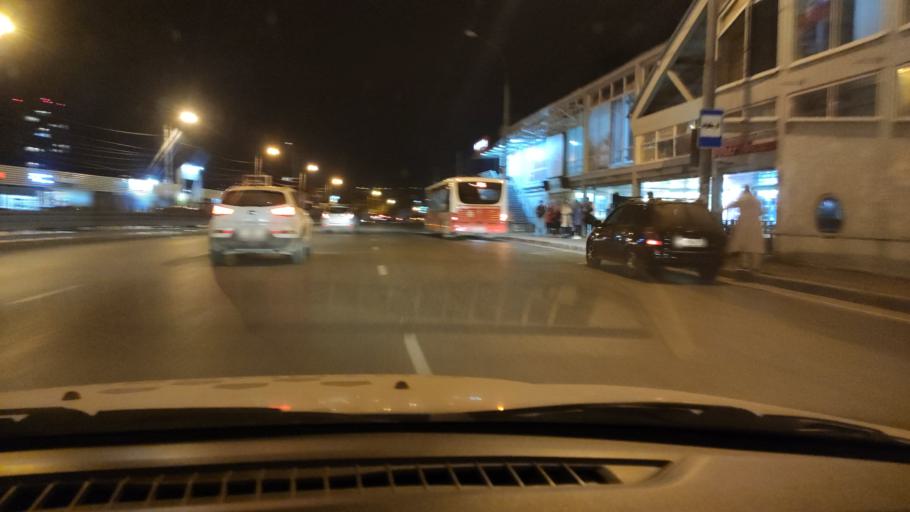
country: RU
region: Perm
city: Perm
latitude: 58.0024
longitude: 56.2309
